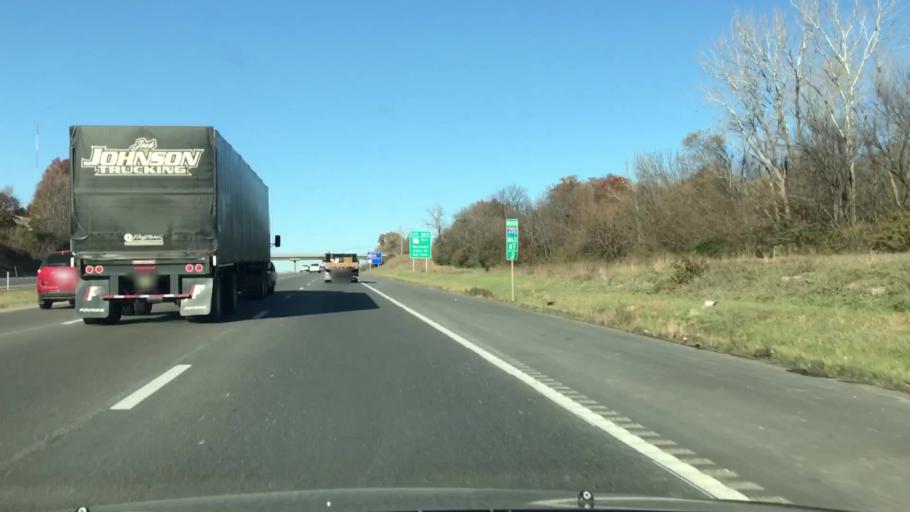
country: US
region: Missouri
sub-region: Jackson County
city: Raytown
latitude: 39.0001
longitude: -94.5019
